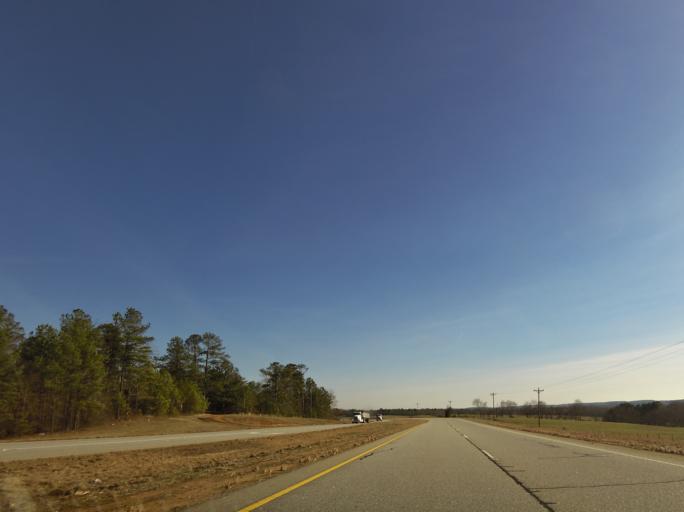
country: US
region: Georgia
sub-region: Upson County
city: Thomaston
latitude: 32.7530
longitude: -84.2431
